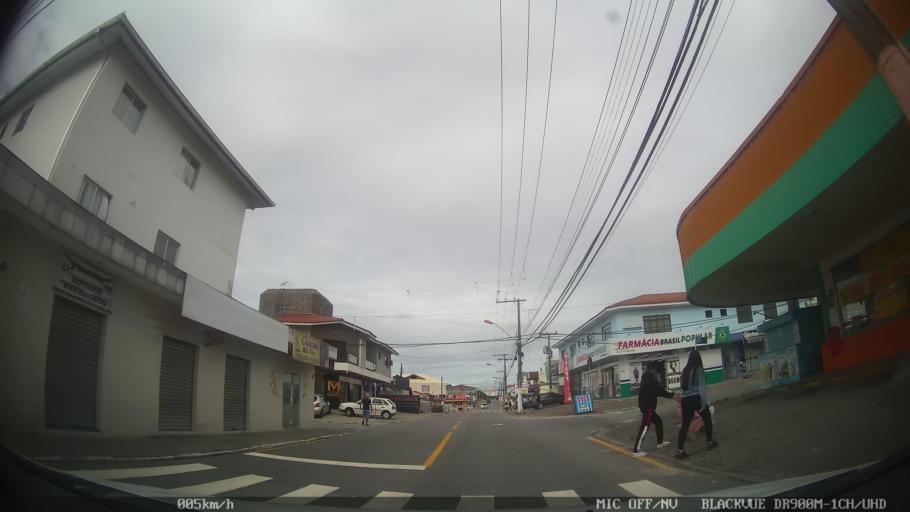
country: BR
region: Santa Catarina
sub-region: Sao Jose
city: Campinas
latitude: -27.5760
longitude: -48.6224
